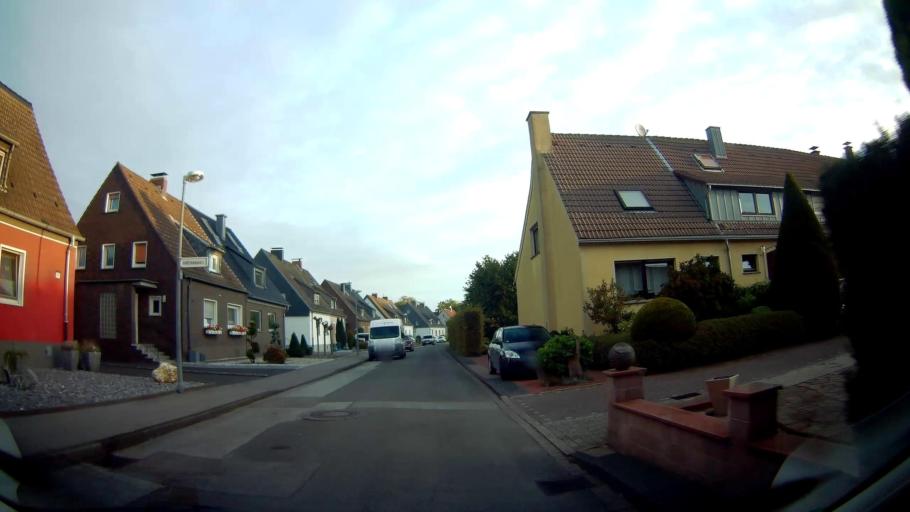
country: DE
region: North Rhine-Westphalia
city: Herten
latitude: 51.6188
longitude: 7.1374
